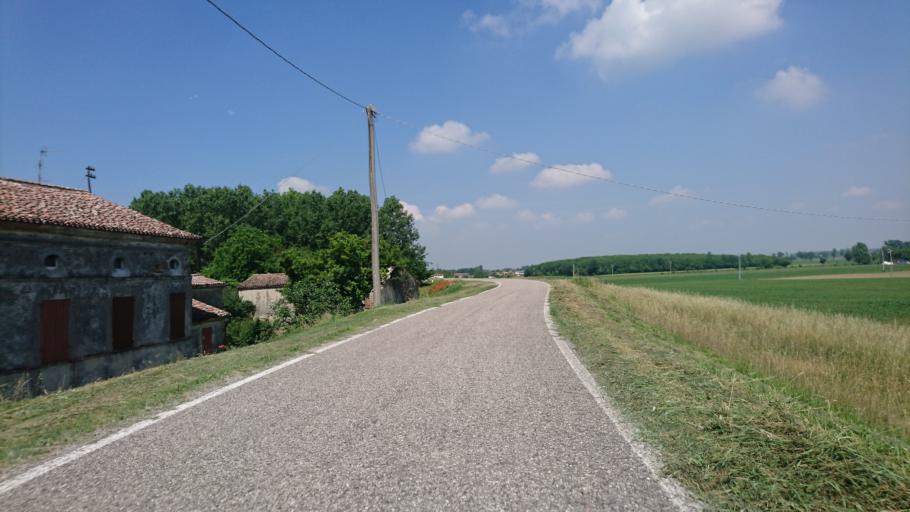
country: IT
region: Lombardy
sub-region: Provincia di Mantova
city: Sustinente
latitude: 45.0772
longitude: 10.9730
